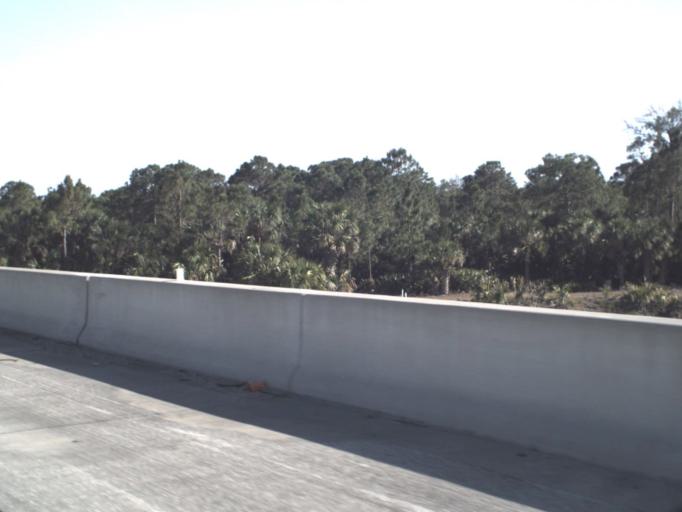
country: US
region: Florida
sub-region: Indian River County
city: Roseland
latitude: 27.8262
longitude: -80.5586
